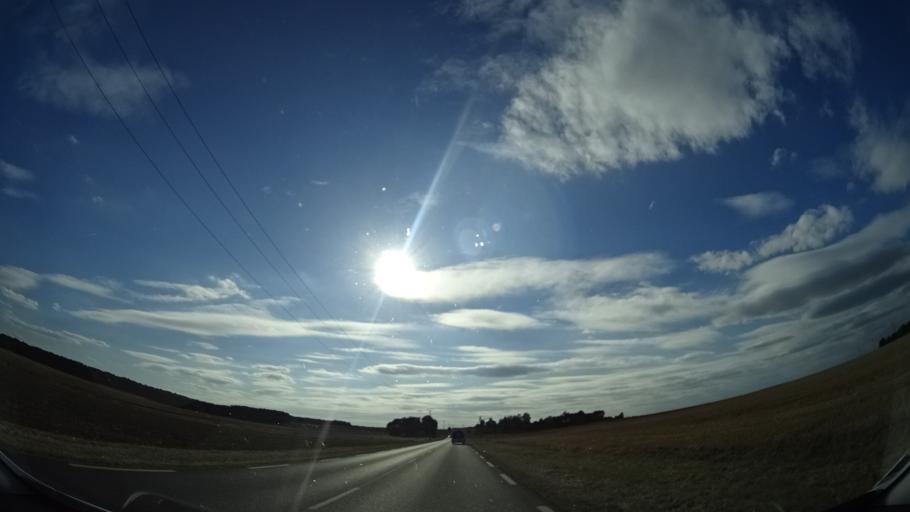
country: FR
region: Centre
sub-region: Departement du Loir-et-Cher
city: Oucques
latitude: 47.9043
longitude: 1.3559
